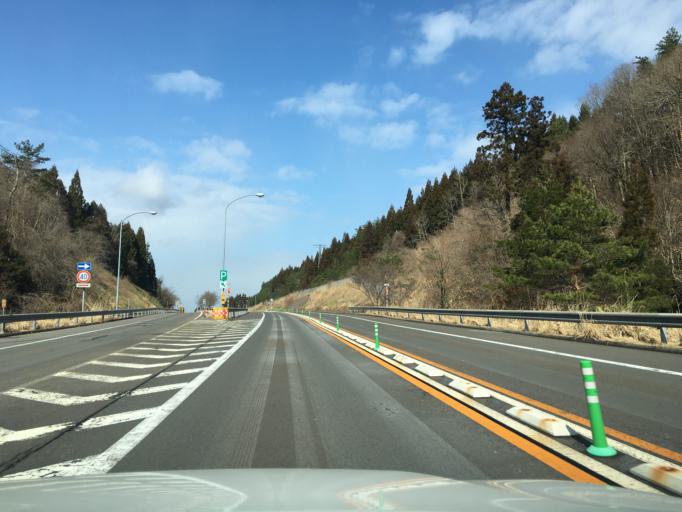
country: JP
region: Akita
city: Akita
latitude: 39.7474
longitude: 140.1558
